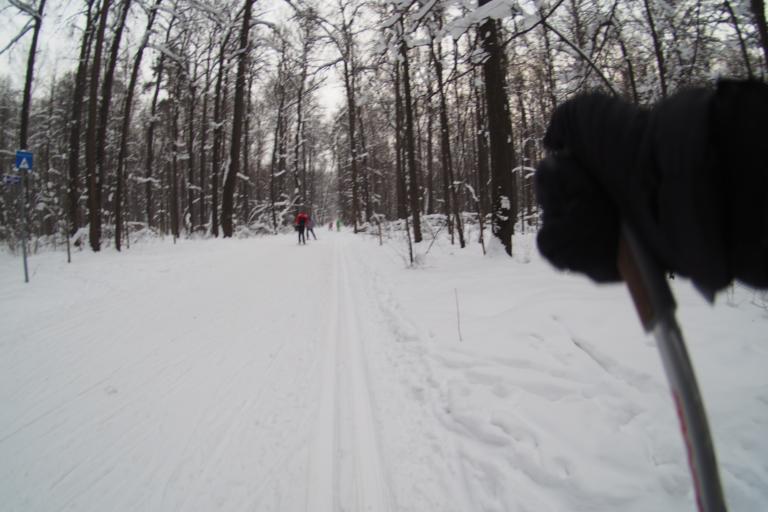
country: RU
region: Moskovskaya
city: Izmaylovo
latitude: 55.7695
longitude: 37.7774
